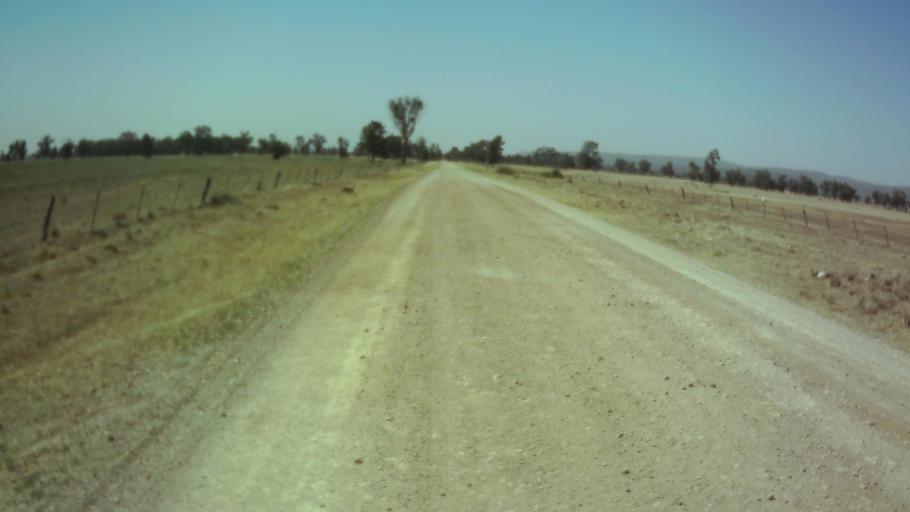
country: AU
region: New South Wales
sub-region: Weddin
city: Grenfell
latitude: -34.0278
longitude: 147.9131
